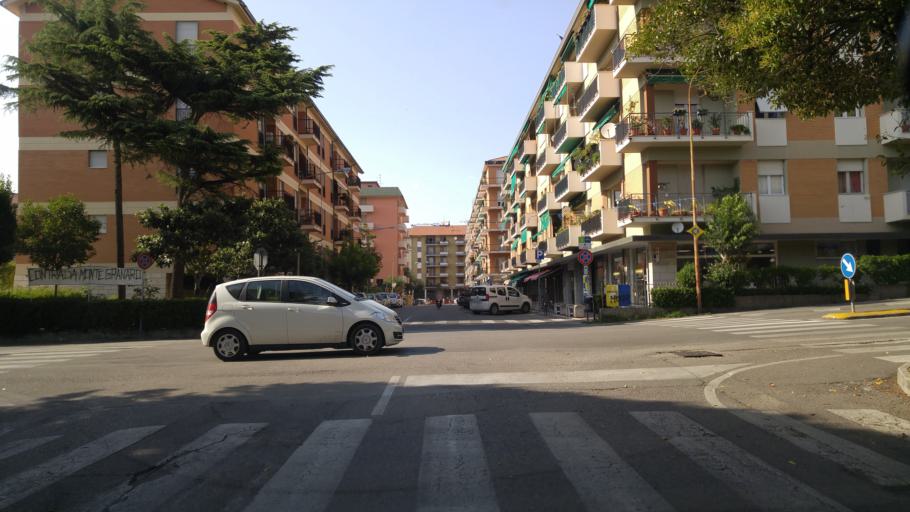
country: IT
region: The Marches
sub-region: Provincia di Pesaro e Urbino
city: Pesaro
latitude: 43.8977
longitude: 12.9230
